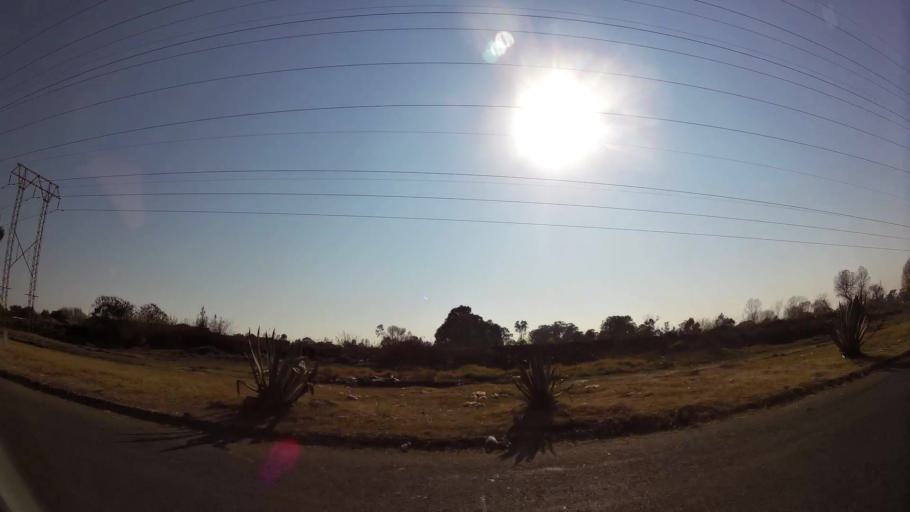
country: ZA
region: Gauteng
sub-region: Ekurhuleni Metropolitan Municipality
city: Boksburg
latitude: -26.2255
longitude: 28.2317
